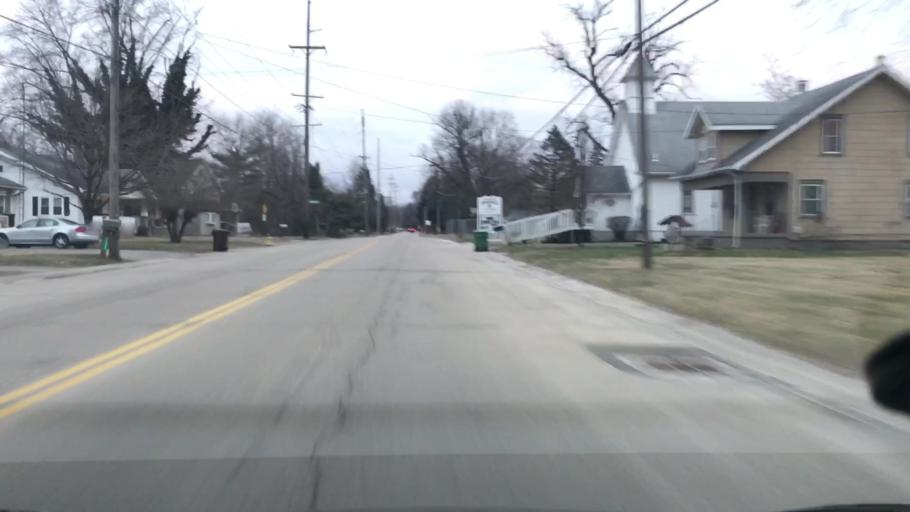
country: US
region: Ohio
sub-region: Clark County
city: Springfield
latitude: 39.9375
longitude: -83.7595
